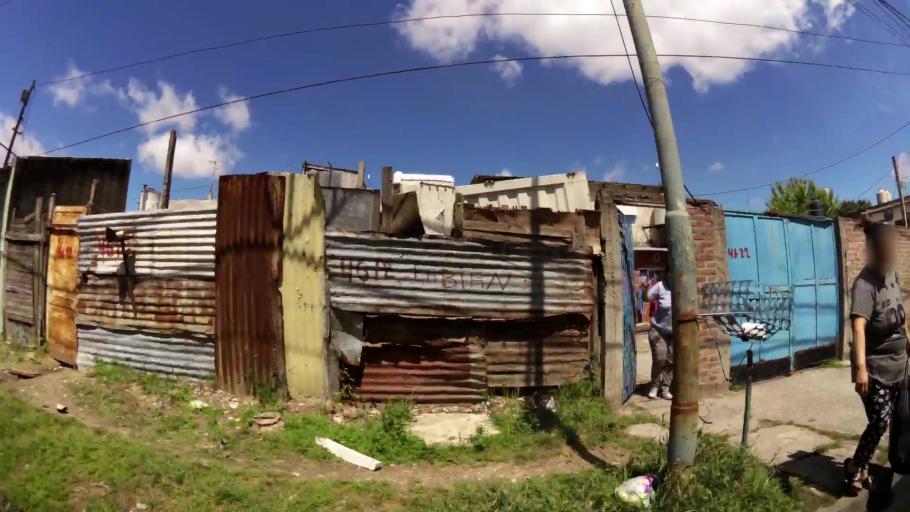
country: AR
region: Buenos Aires
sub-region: Partido de Lanus
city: Lanus
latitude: -34.6947
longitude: -58.4322
